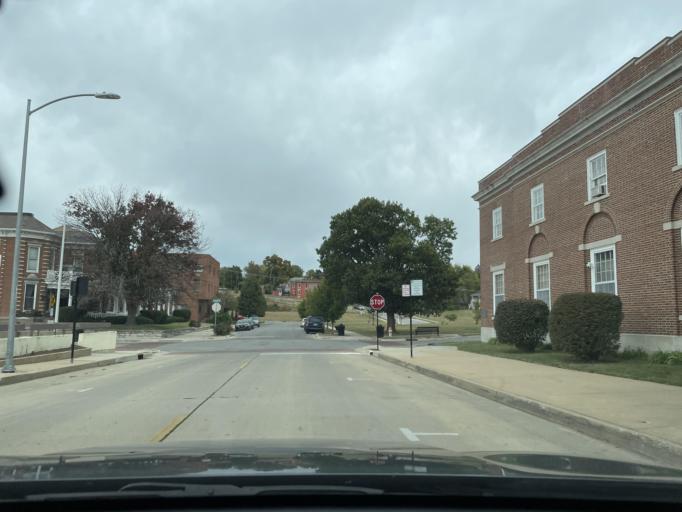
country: US
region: Missouri
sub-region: Buchanan County
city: Saint Joseph
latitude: 39.7687
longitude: -94.8519
